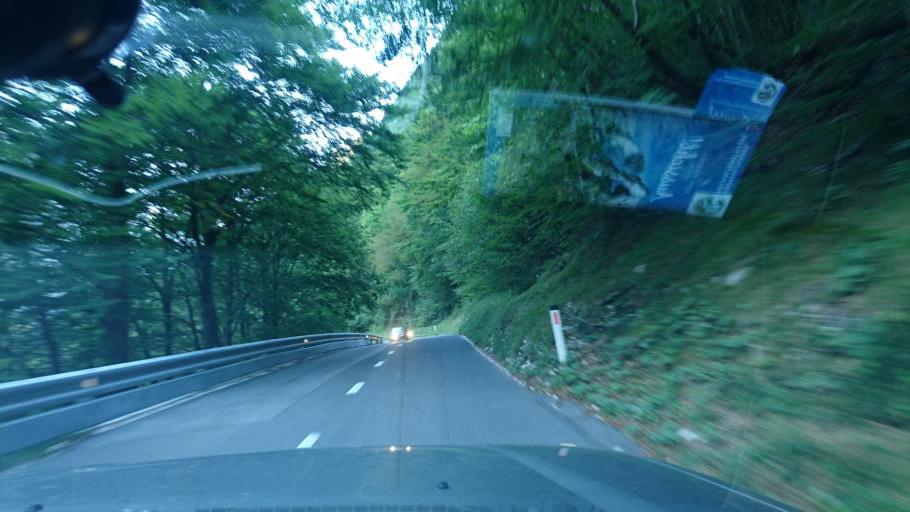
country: SI
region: Bovec
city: Bovec
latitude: 46.3656
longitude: 13.5864
